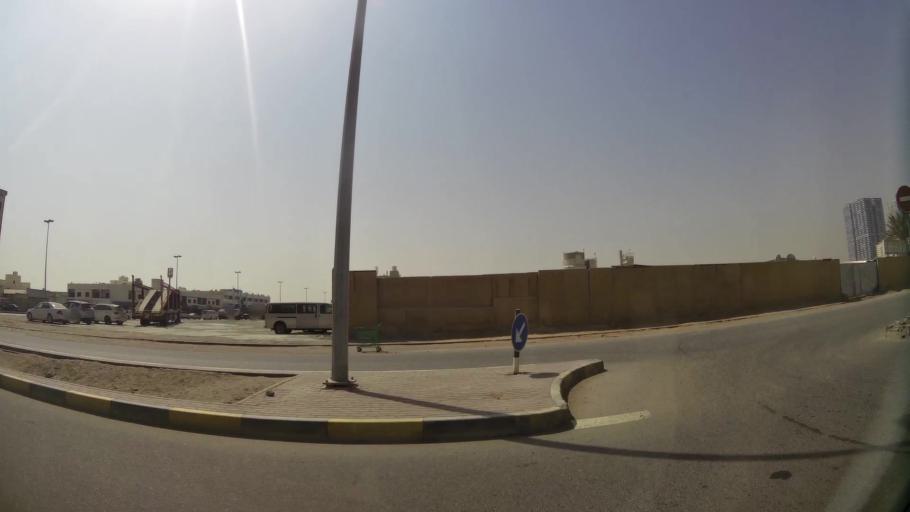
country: AE
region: Ash Shariqah
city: Sharjah
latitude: 25.3108
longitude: 55.3860
